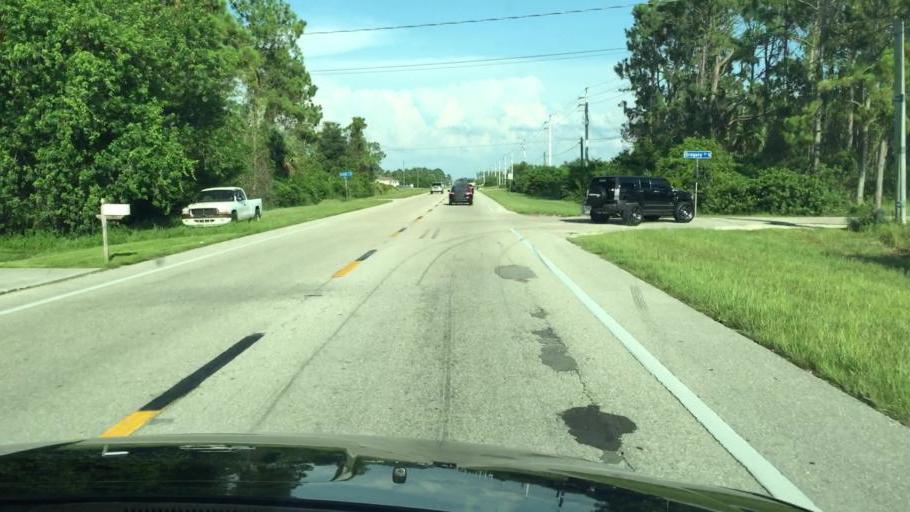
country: US
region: Florida
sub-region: Lee County
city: Gateway
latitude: 26.5958
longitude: -81.7265
